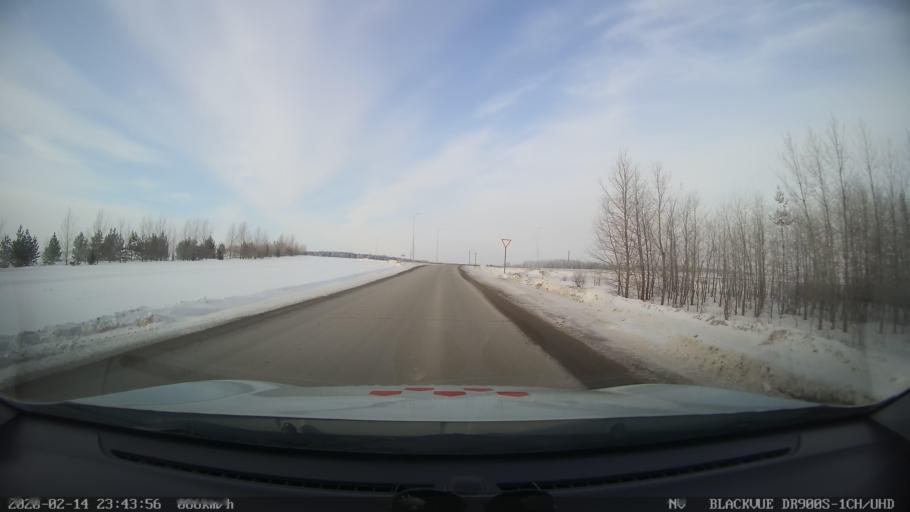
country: RU
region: Tatarstan
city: Kuybyshevskiy Zaton
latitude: 55.2080
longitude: 49.2474
